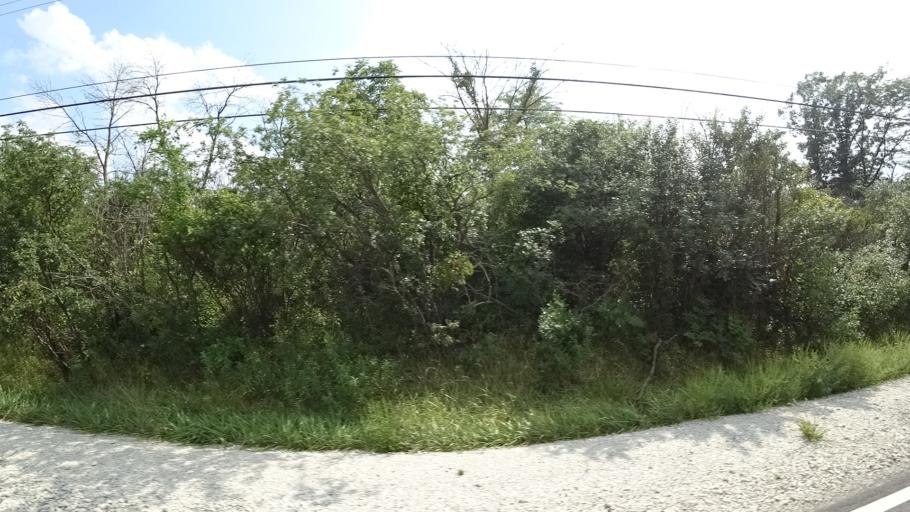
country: US
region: Illinois
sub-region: Will County
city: Goodings Grove
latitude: 41.6659
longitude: -87.9054
